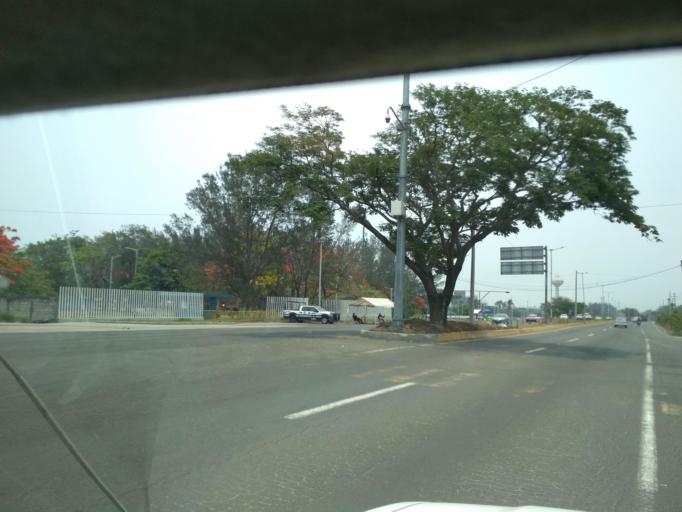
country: MX
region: Veracruz
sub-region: Veracruz
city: Oasis
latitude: 19.1788
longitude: -96.2489
